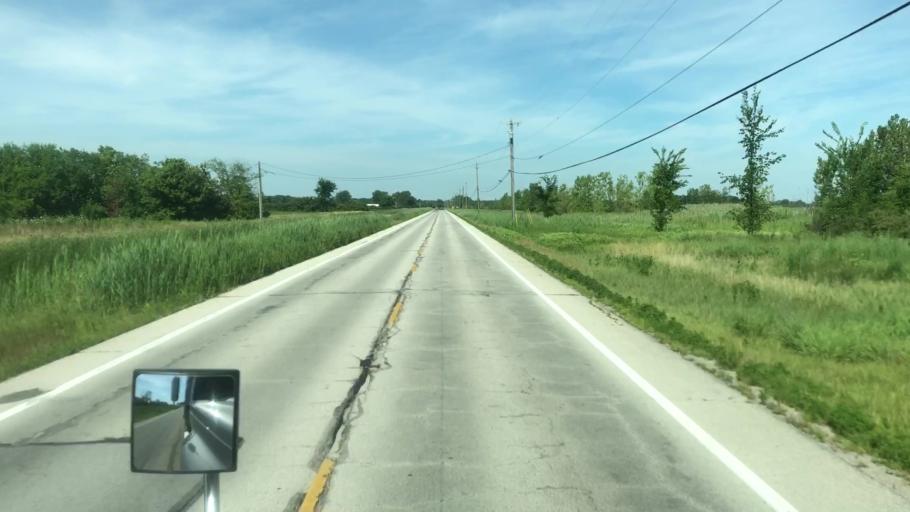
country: US
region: Ohio
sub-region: Ottawa County
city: Port Clinton
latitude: 41.4086
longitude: -82.9214
